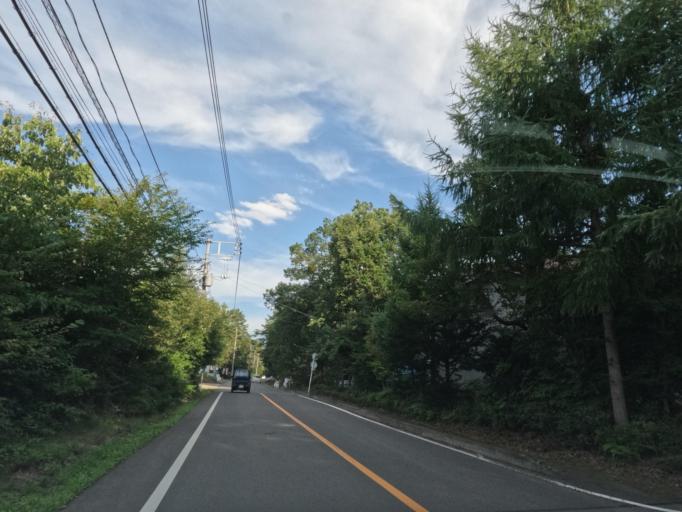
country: JP
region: Nagano
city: Komoro
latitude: 36.4463
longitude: 138.5729
